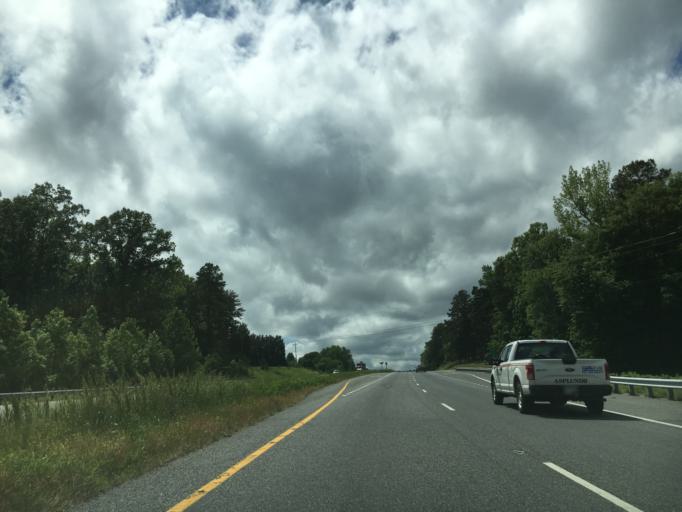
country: US
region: Virginia
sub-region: Mecklenburg County
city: Clarksville
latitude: 36.6510
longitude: -78.4830
